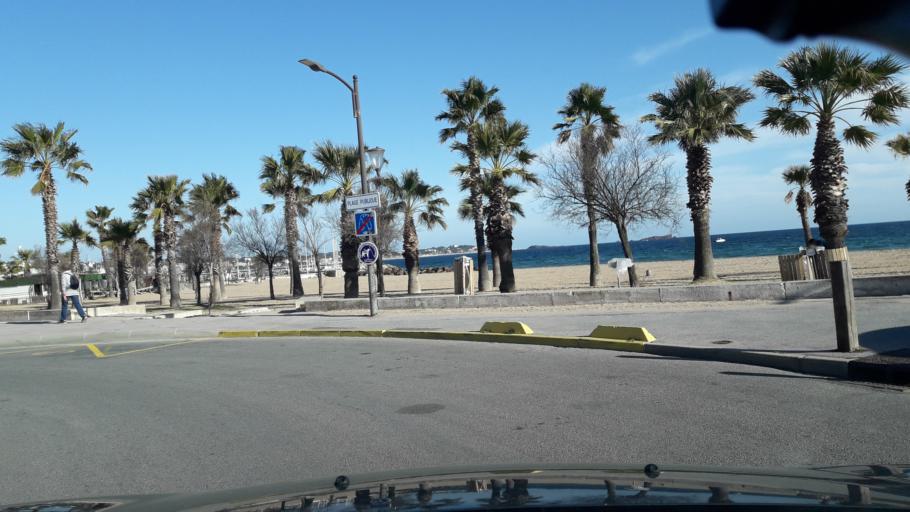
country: FR
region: Provence-Alpes-Cote d'Azur
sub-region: Departement du Var
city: Frejus
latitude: 43.4189
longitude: 6.7462
